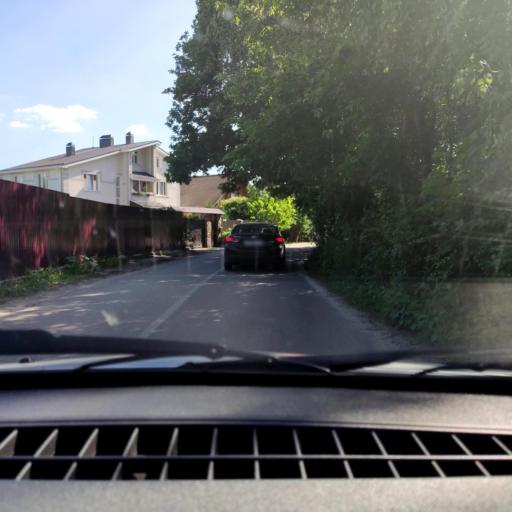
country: RU
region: Voronezj
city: Ramon'
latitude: 51.8208
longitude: 39.2663
